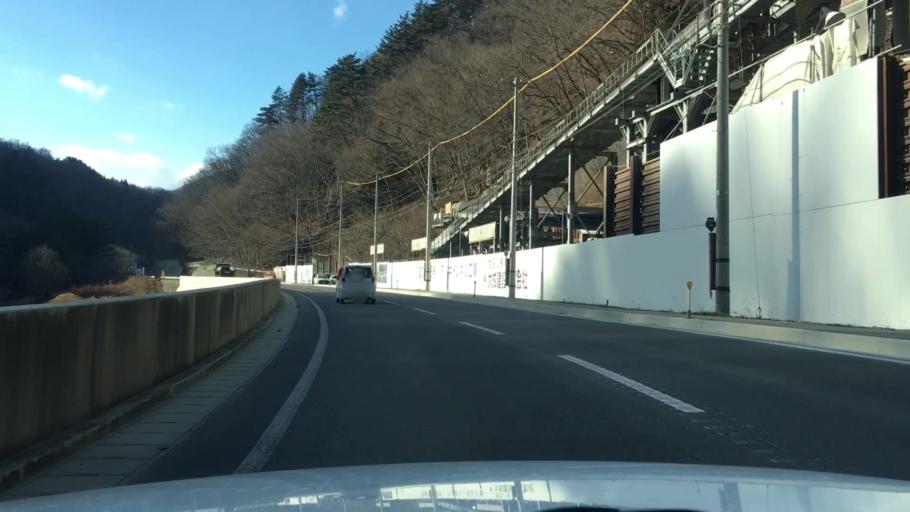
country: JP
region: Iwate
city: Miyako
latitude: 39.6014
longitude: 141.7105
